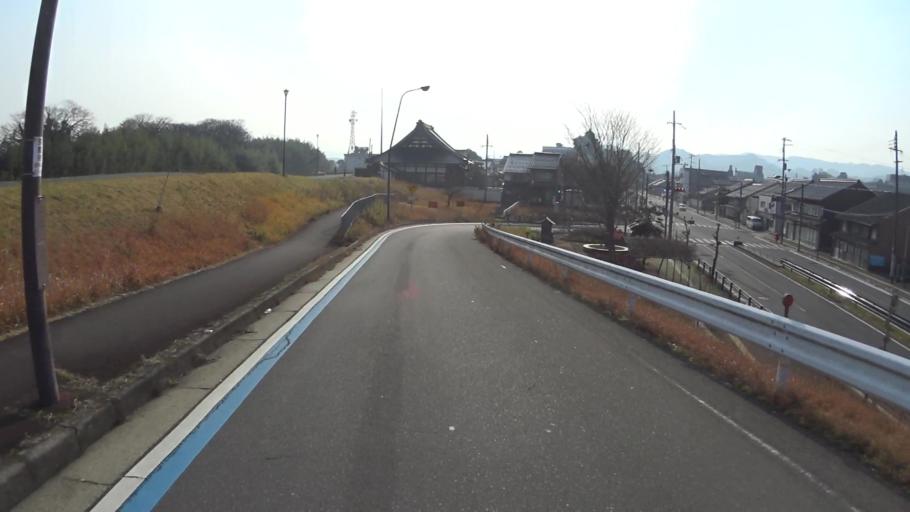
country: JP
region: Kyoto
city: Fukuchiyama
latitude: 35.3010
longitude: 135.1285
